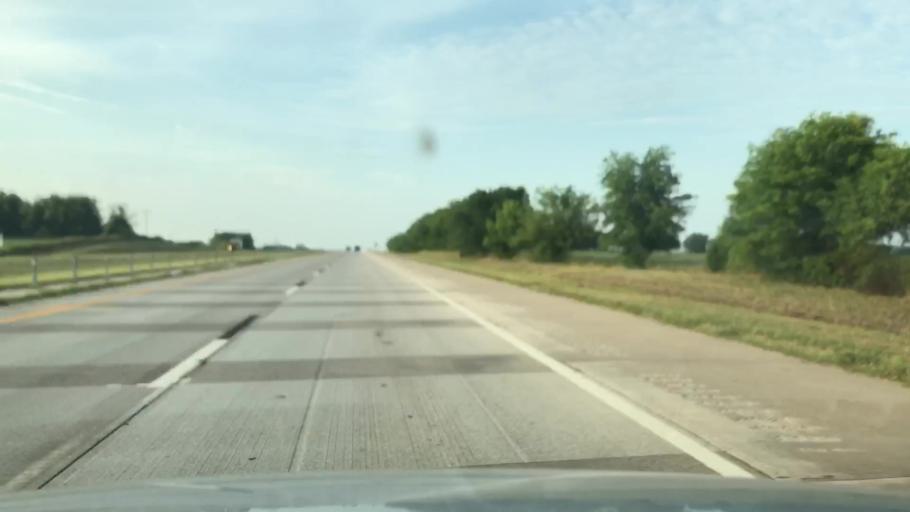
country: US
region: Oklahoma
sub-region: Osage County
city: Skiatook
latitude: 36.4292
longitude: -95.9209
